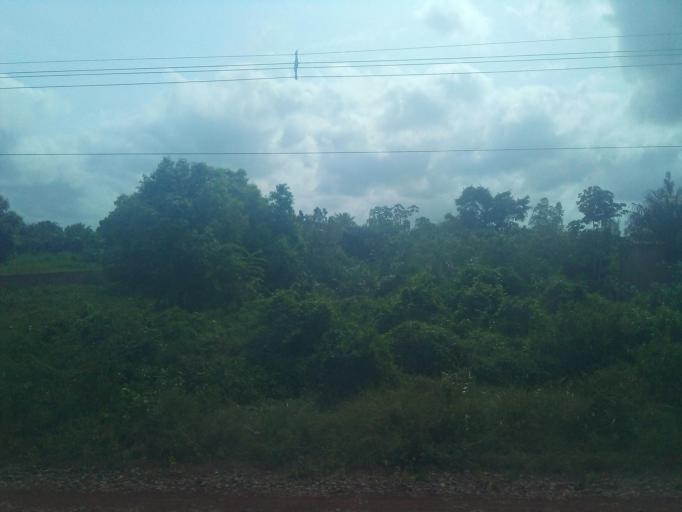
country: BR
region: Maranhao
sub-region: Icatu
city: Icatu
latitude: -2.9427
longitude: -44.3460
